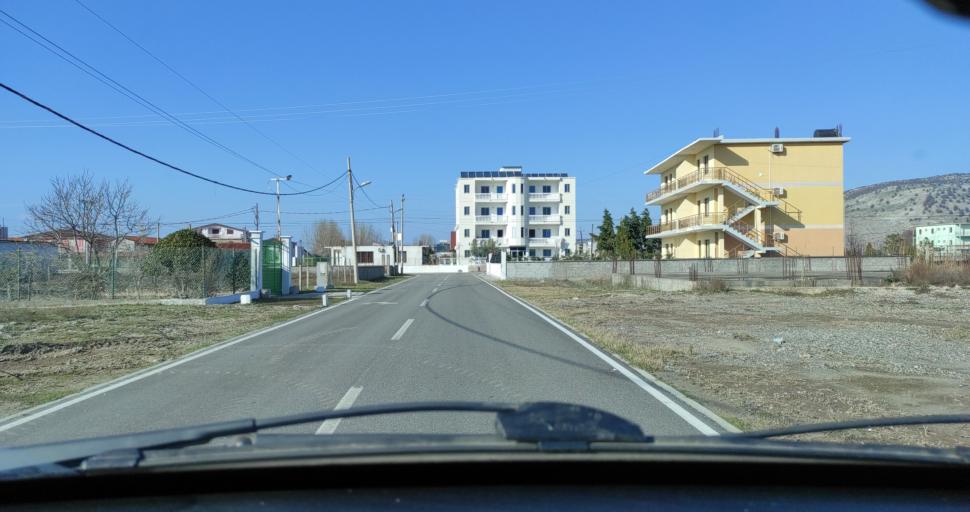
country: AL
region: Shkoder
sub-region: Rrethi i Shkodres
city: Velipoje
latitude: 41.8649
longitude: 19.4337
